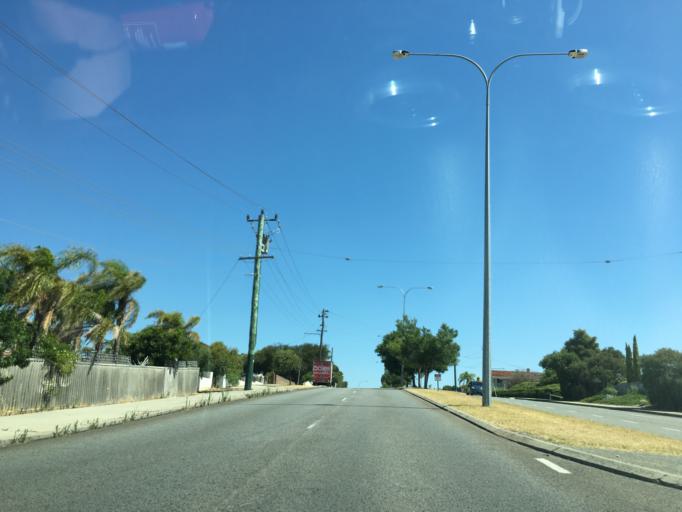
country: AU
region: Western Australia
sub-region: Canning
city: Willetton
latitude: -32.0488
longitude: 115.9042
